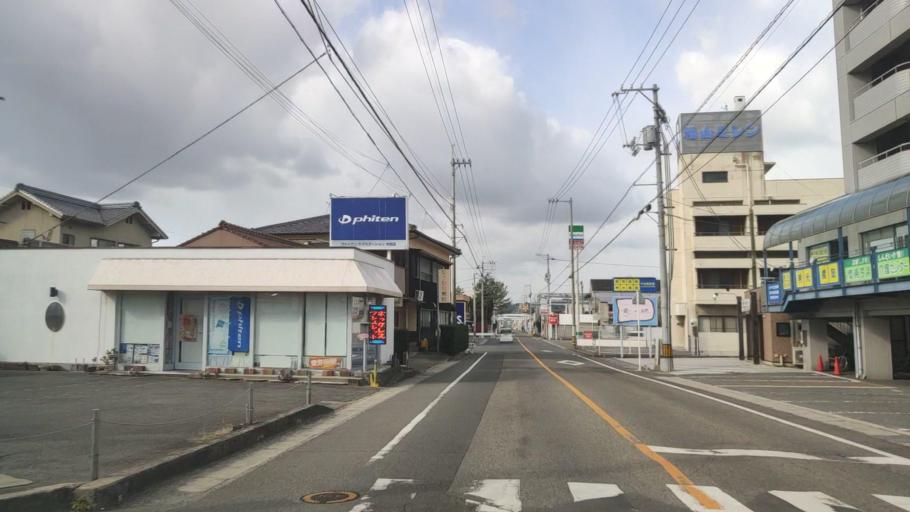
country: JP
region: Ehime
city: Saijo
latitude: 34.0487
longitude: 133.0166
